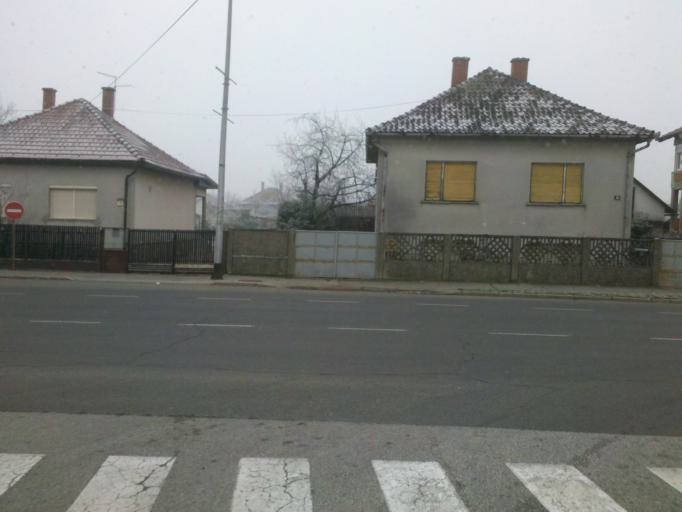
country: HR
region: Medimurska
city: Cakovec
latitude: 46.3826
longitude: 16.4302
